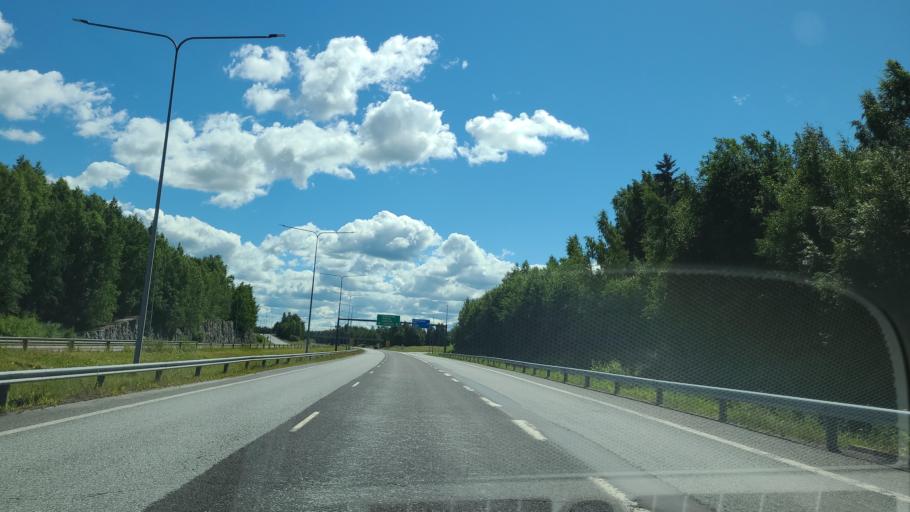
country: FI
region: Ostrobothnia
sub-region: Vaasa
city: Ristinummi
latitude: 63.0315
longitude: 21.7475
